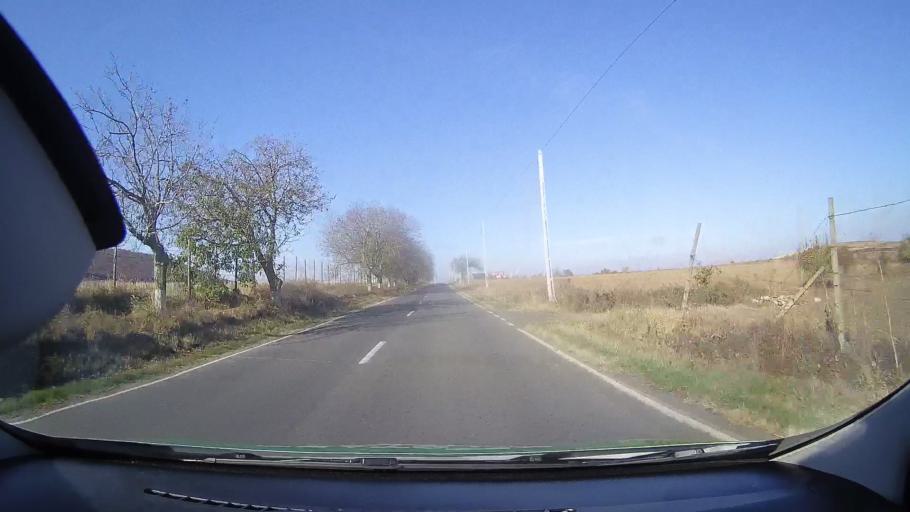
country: RO
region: Tulcea
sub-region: Oras Babadag
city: Babadag
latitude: 44.8824
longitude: 28.7426
